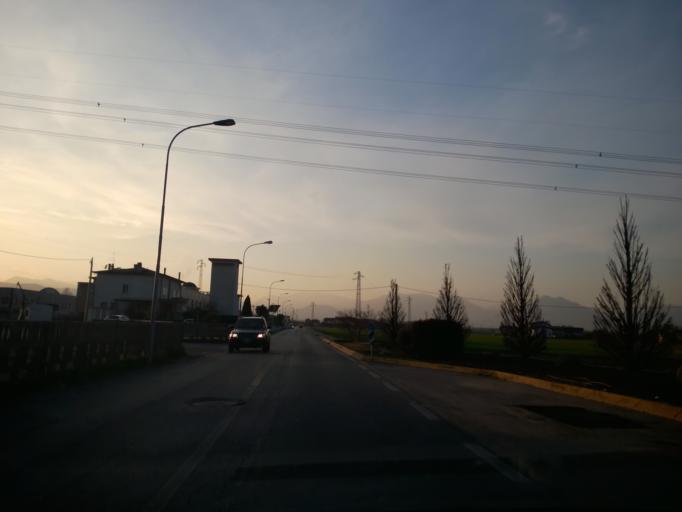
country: IT
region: Veneto
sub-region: Provincia di Vicenza
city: Novoledo
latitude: 45.6284
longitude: 11.5001
